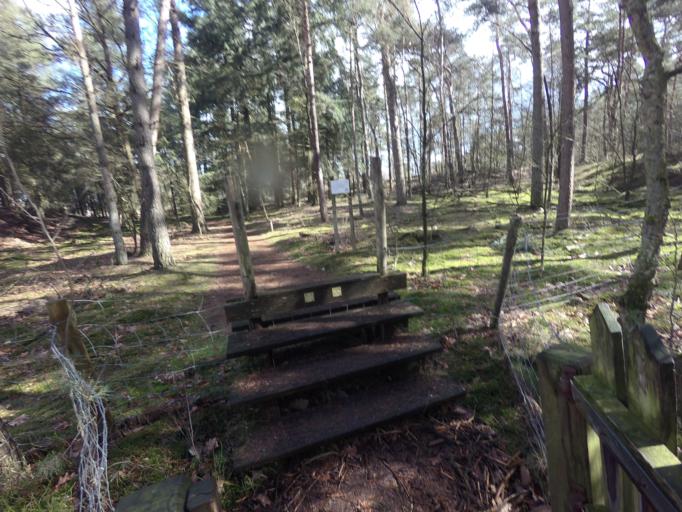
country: NL
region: Utrecht
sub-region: Gemeente Utrechtse Heuvelrug
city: Driebergen-Rijsenburg
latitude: 52.0711
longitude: 5.2801
